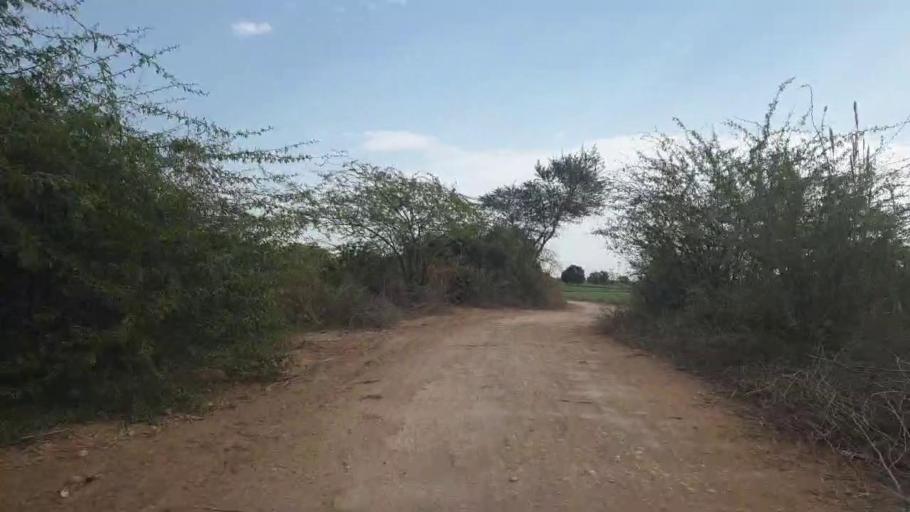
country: PK
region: Sindh
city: Sakrand
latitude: 25.9988
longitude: 68.3357
